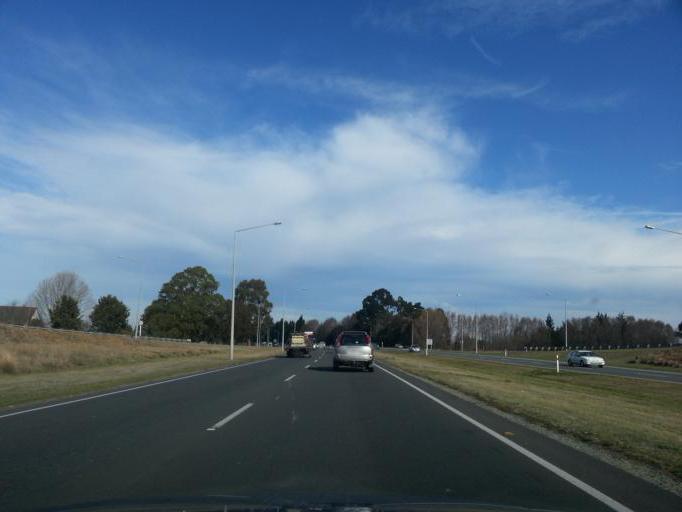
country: NZ
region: Canterbury
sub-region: Waimakariri District
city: Kaiapoi
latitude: -43.3871
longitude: 172.6409
